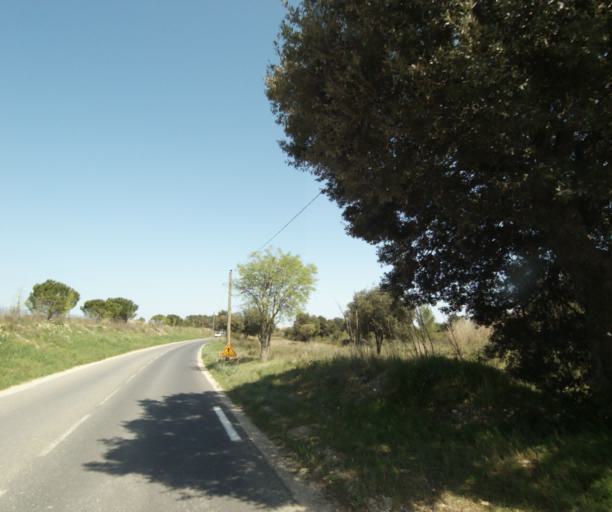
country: FR
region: Languedoc-Roussillon
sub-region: Departement de l'Herault
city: Combaillaux
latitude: 43.6445
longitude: 3.7634
